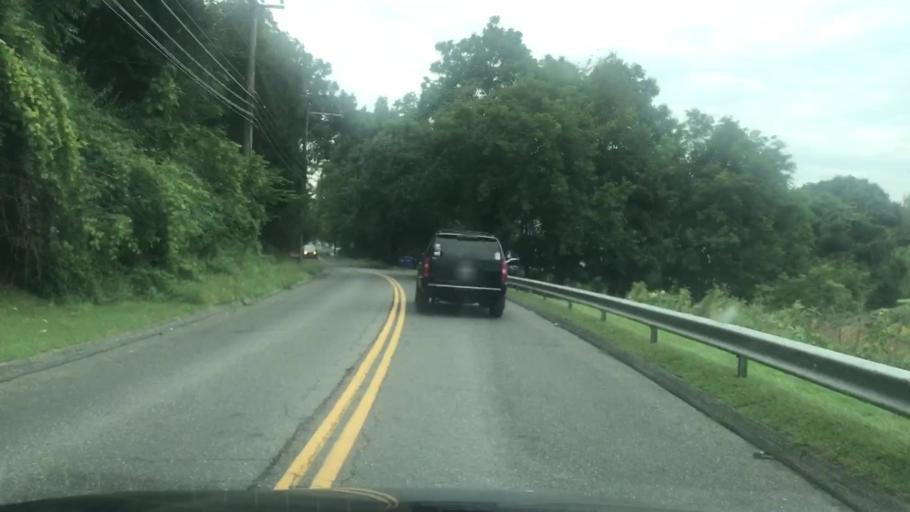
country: US
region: Connecticut
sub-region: Litchfield County
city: New Milford
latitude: 41.5933
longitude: -73.4175
